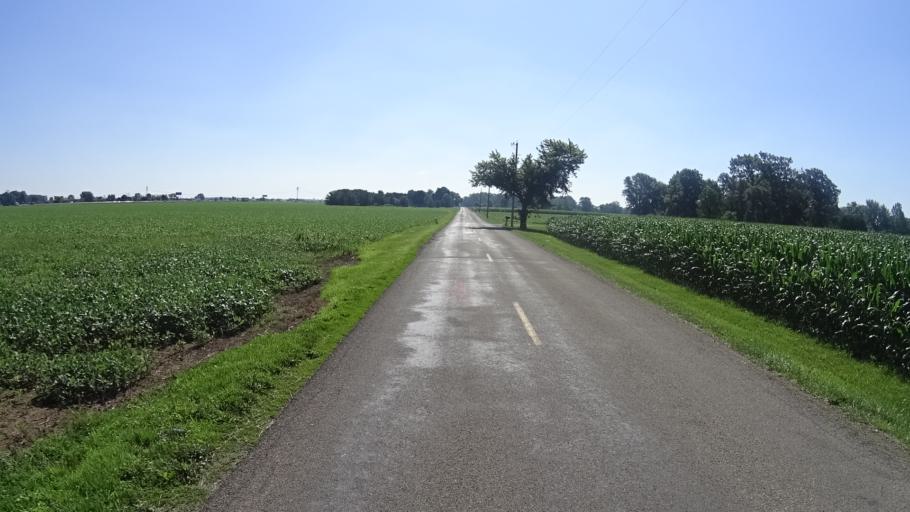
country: US
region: Indiana
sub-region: Madison County
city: Ingalls
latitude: 39.9878
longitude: -85.8339
